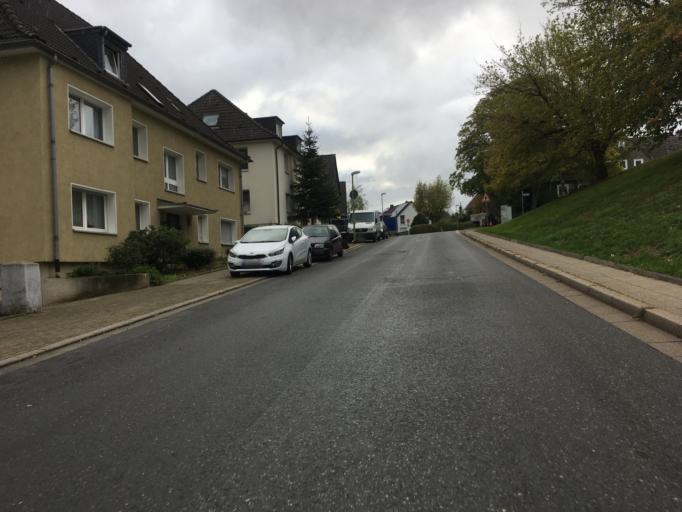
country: DE
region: North Rhine-Westphalia
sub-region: Regierungsbezirk Munster
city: Bottrop
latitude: 51.4806
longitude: 6.9348
